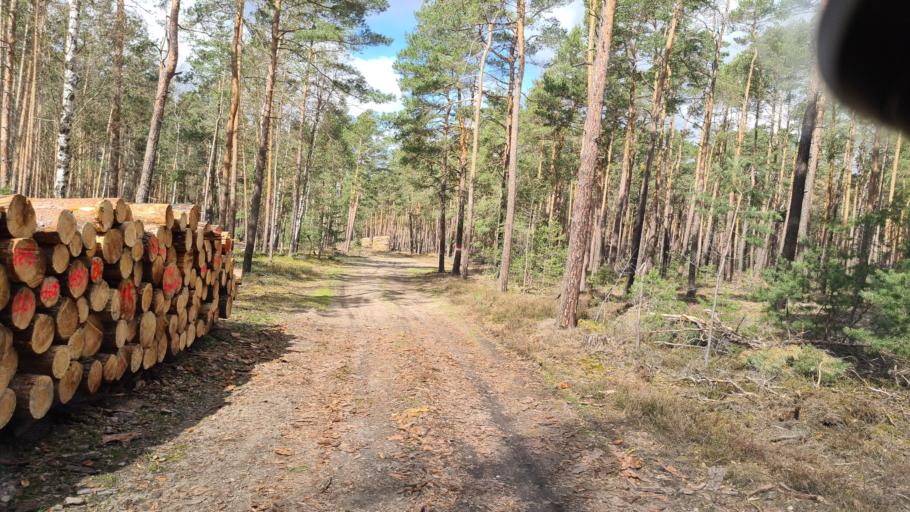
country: DE
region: Brandenburg
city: Schonborn
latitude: 51.6524
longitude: 13.4712
